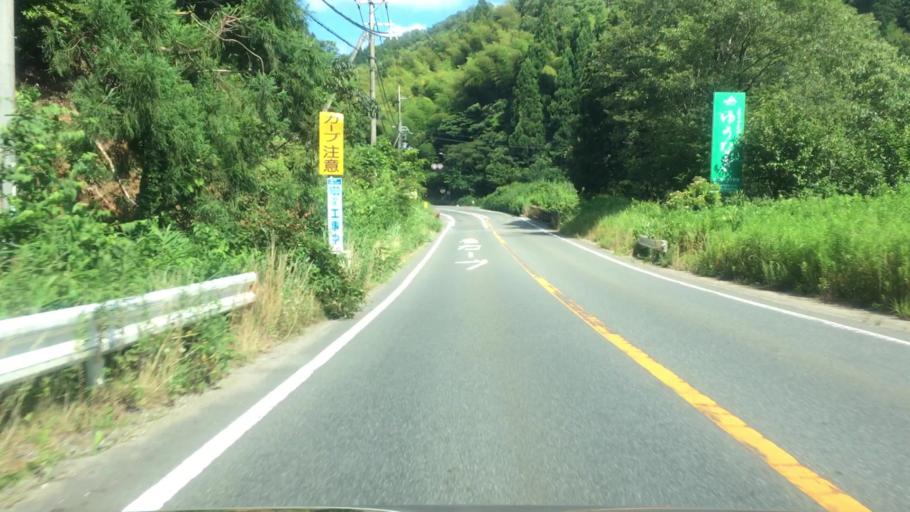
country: JP
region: Hyogo
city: Toyooka
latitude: 35.5730
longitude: 134.7747
